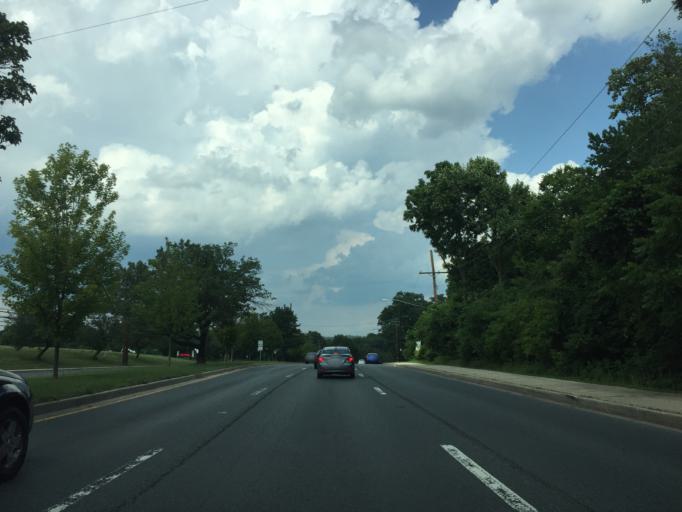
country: US
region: Maryland
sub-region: Montgomery County
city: Glenmont
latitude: 39.0642
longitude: -77.0388
